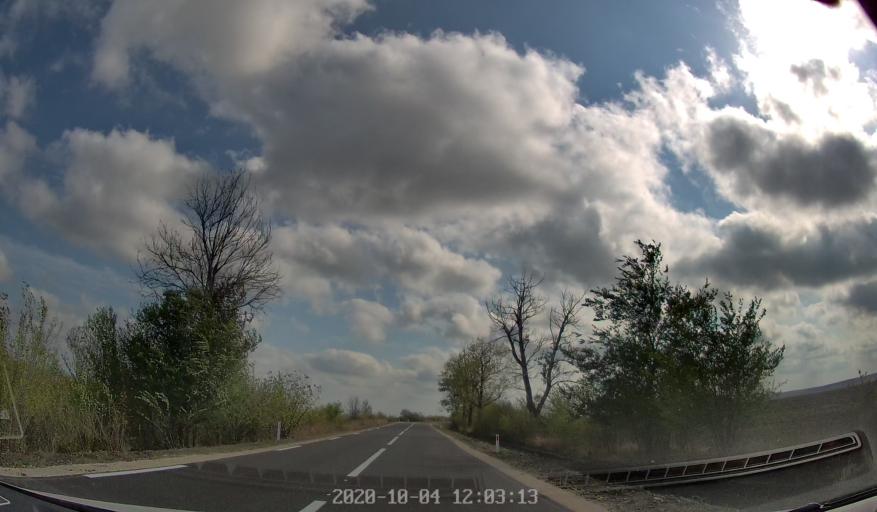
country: MD
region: Rezina
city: Saharna
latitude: 47.6133
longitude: 28.9226
